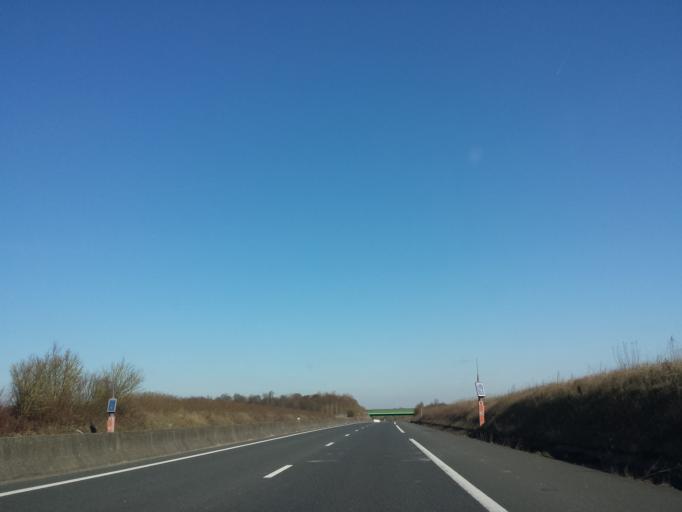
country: FR
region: Picardie
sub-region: Departement de l'Oise
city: Breteuil
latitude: 49.5710
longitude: 2.1994
